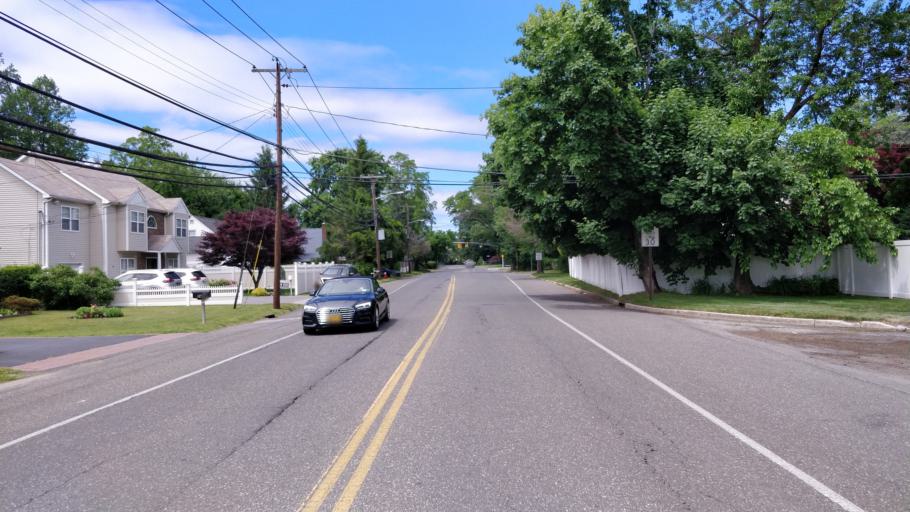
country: US
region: New York
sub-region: Suffolk County
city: South Huntington
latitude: 40.8120
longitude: -73.4075
